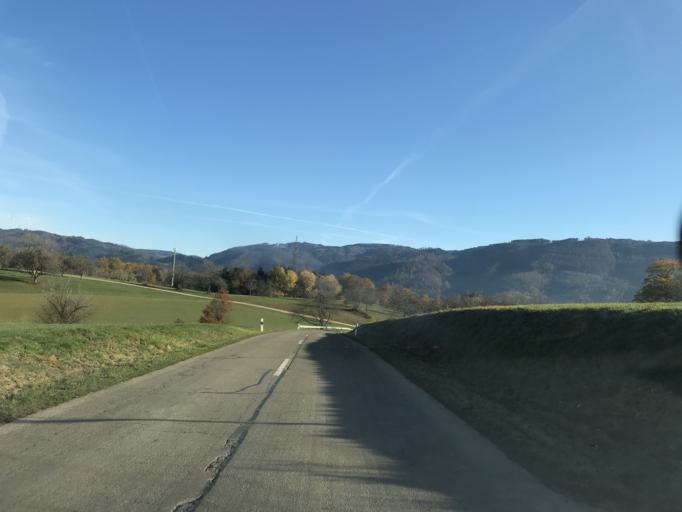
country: DE
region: Baden-Wuerttemberg
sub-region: Freiburg Region
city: Wehr
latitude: 47.6246
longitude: 7.8842
